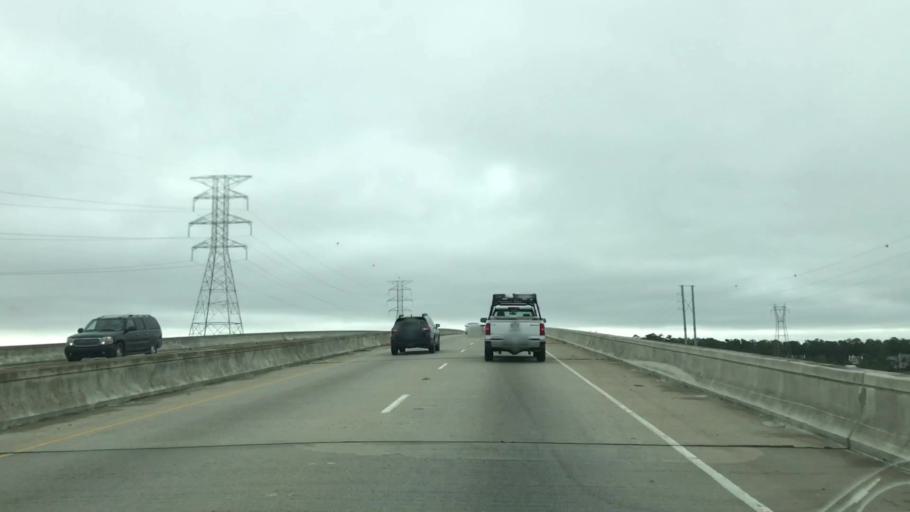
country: US
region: South Carolina
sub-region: Beaufort County
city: Hilton Head Island
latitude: 32.2267
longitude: -80.7834
